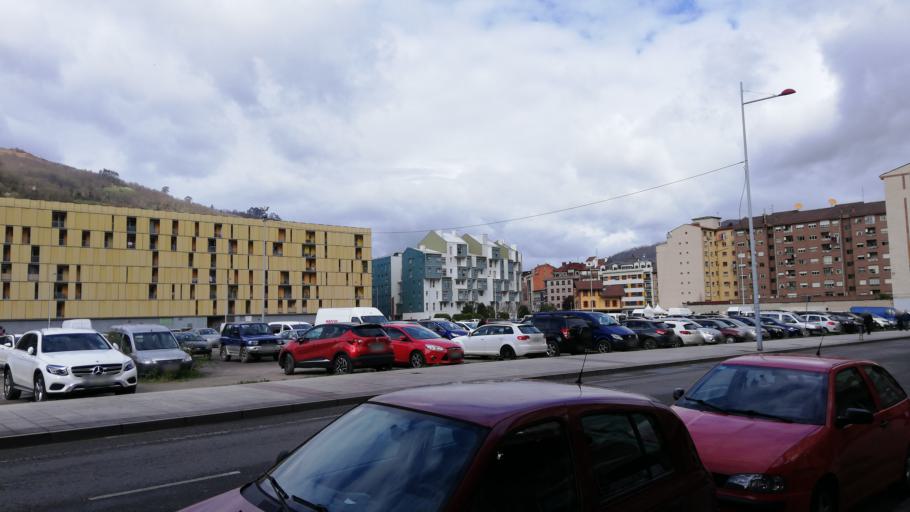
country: ES
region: Asturias
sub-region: Province of Asturias
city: Mieres
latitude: 43.2485
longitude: -5.7765
